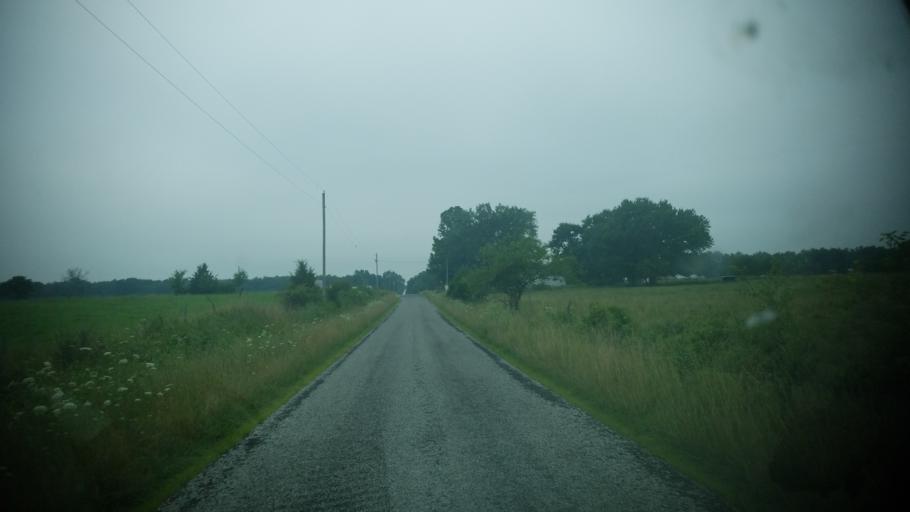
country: US
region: Illinois
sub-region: Clay County
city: Flora
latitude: 38.5735
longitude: -88.3817
